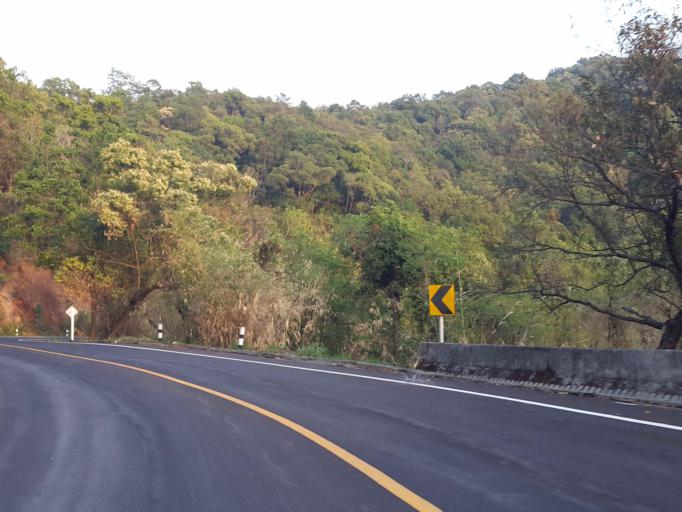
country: TH
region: Chiang Mai
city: Mae On
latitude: 19.0079
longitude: 99.3202
